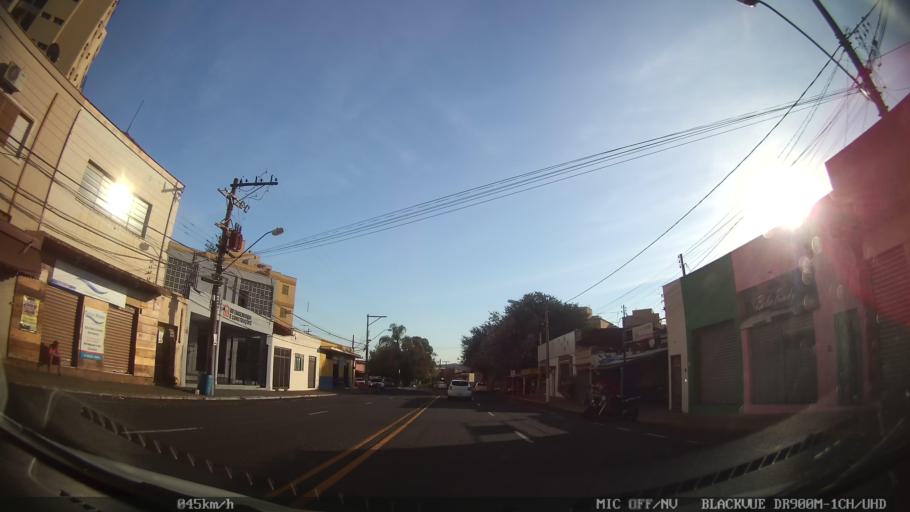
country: BR
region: Sao Paulo
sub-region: Ribeirao Preto
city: Ribeirao Preto
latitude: -21.1881
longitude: -47.8012
